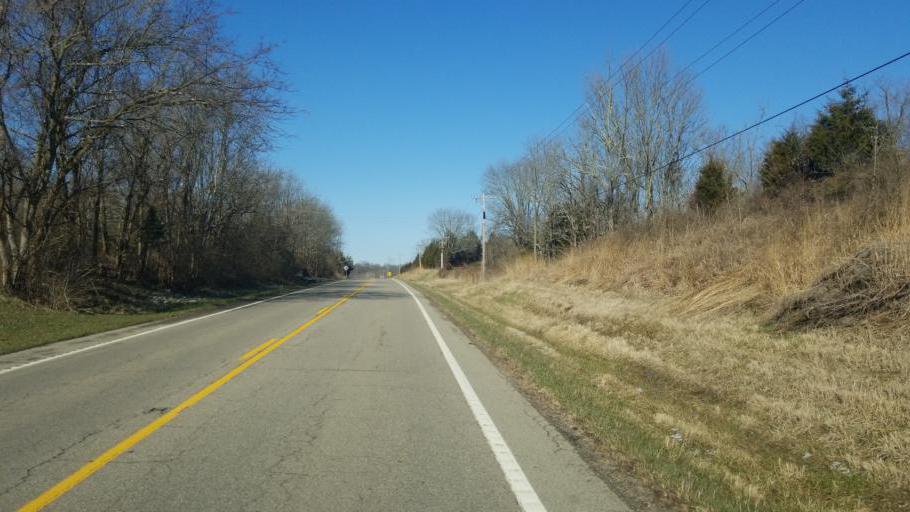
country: US
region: Ohio
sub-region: Highland County
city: Greenfield
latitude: 39.2311
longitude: -83.3347
